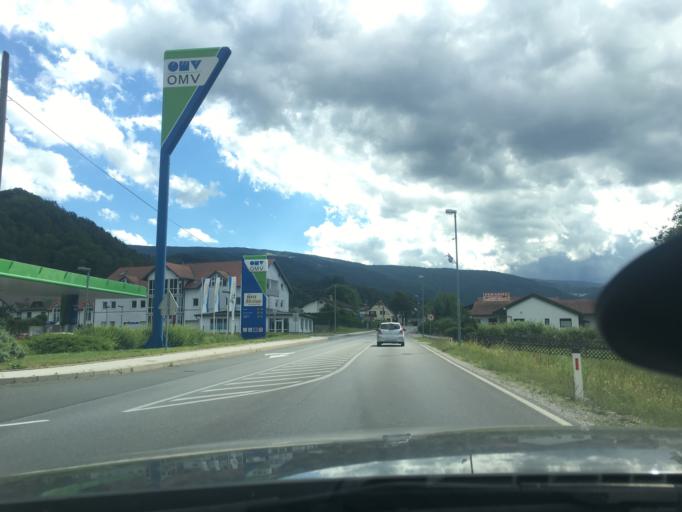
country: SI
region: Ruse
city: Bistrica ob Dravi
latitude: 46.5503
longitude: 15.5381
